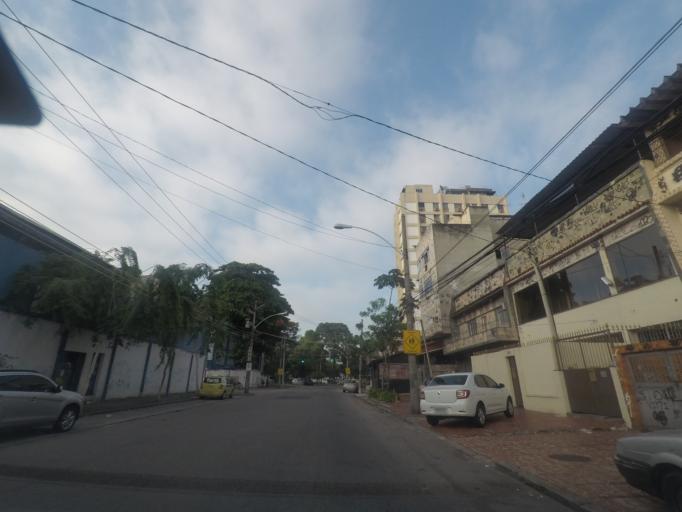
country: BR
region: Rio de Janeiro
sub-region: Duque De Caxias
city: Duque de Caxias
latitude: -22.8414
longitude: -43.2679
